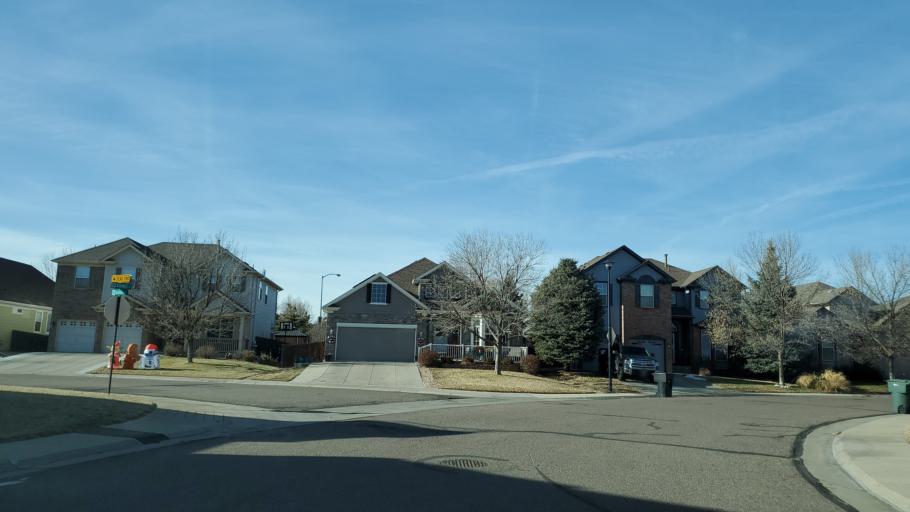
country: US
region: Colorado
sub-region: Adams County
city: Northglenn
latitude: 39.9173
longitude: -104.9487
